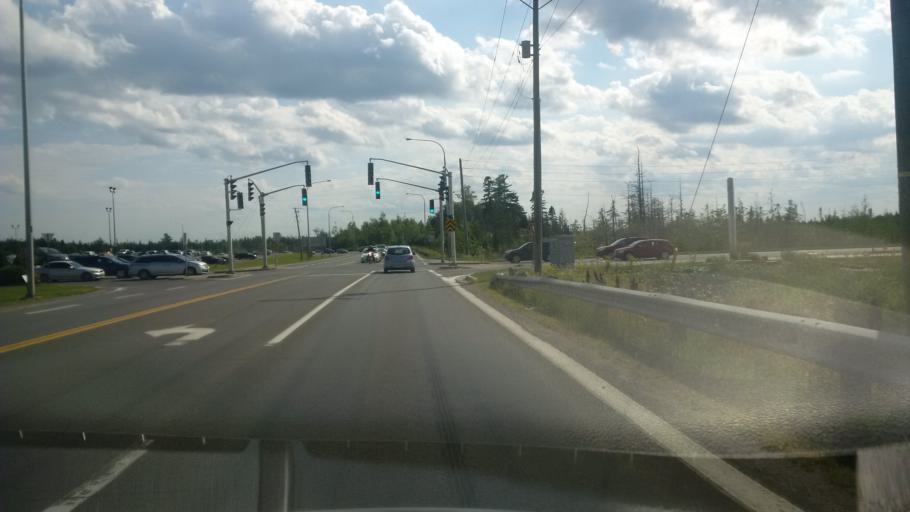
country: CA
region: New Brunswick
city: Fredericton
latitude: 45.9368
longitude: -66.6663
